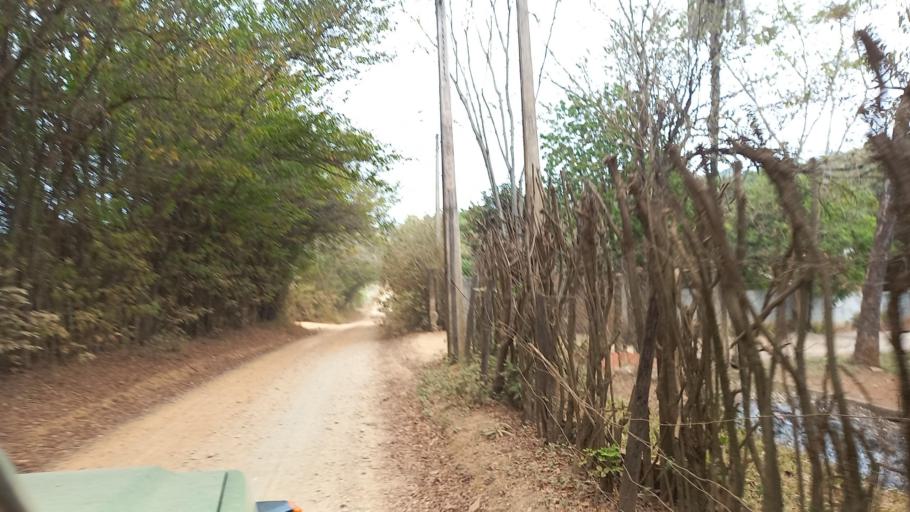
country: BR
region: Sao Paulo
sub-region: Moji-Guacu
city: Mogi-Gaucu
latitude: -22.2954
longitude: -46.8318
